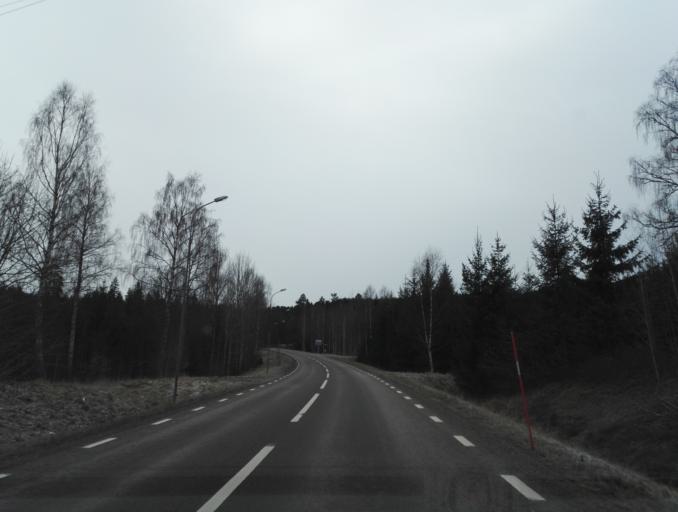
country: SE
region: Kalmar
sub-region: Hultsfreds Kommun
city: Virserum
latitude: 57.3312
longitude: 15.5871
